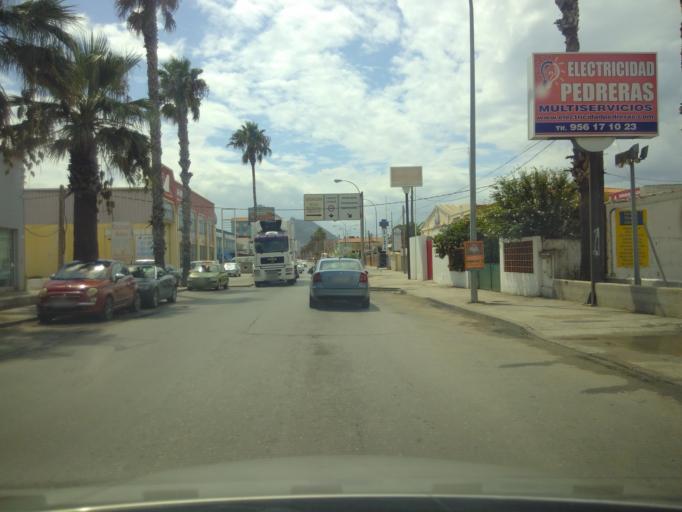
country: ES
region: Andalusia
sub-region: Provincia de Cadiz
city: La Linea de la Concepcion
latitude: 36.1786
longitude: -5.3490
